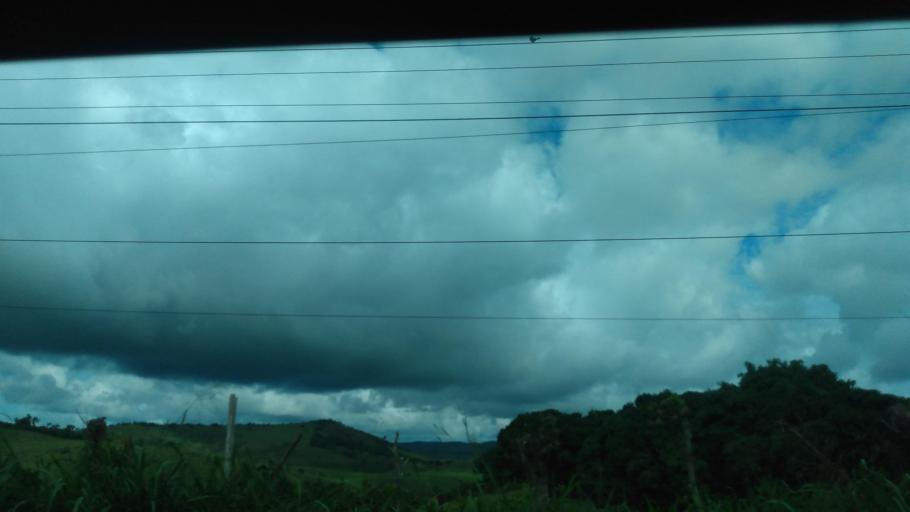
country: BR
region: Pernambuco
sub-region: Quipapa
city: Quipapa
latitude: -8.8109
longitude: -36.0101
